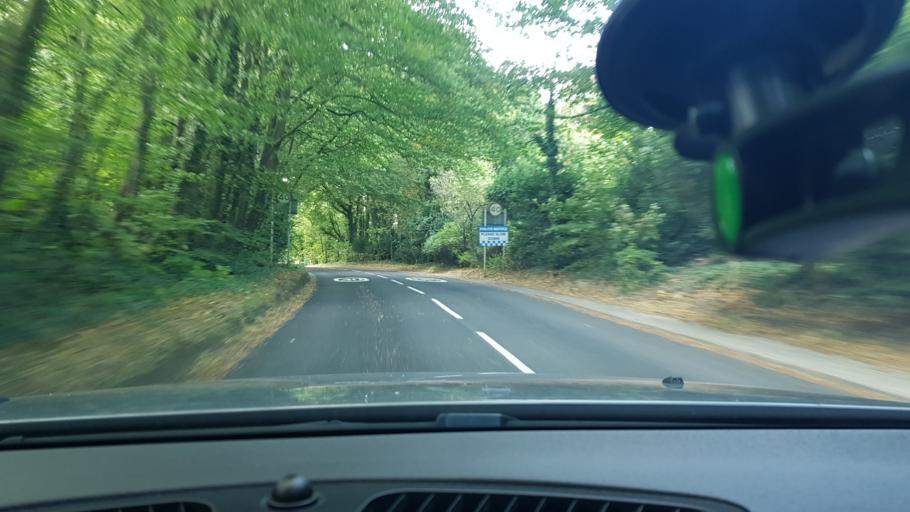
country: GB
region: England
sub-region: West Berkshire
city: Lambourn
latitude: 51.5132
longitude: -1.5373
